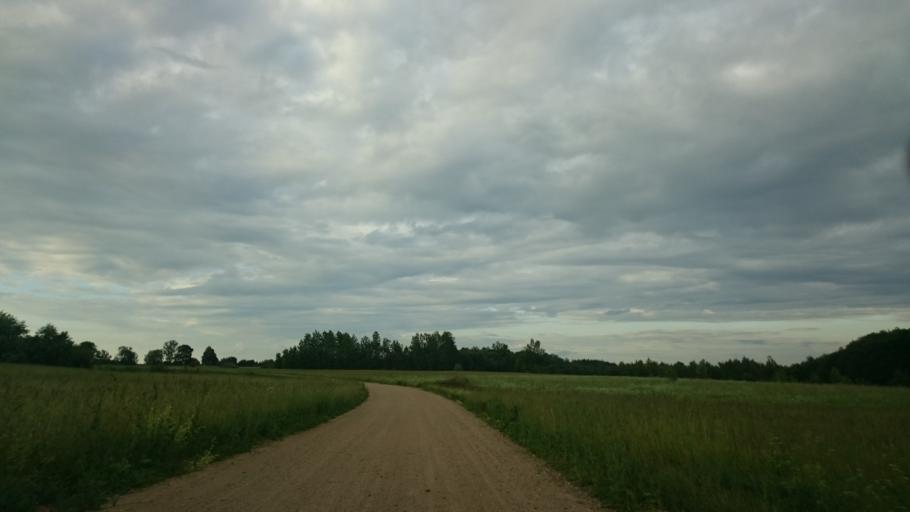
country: LV
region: Ludzas Rajons
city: Ludza
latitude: 56.5444
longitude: 27.6385
